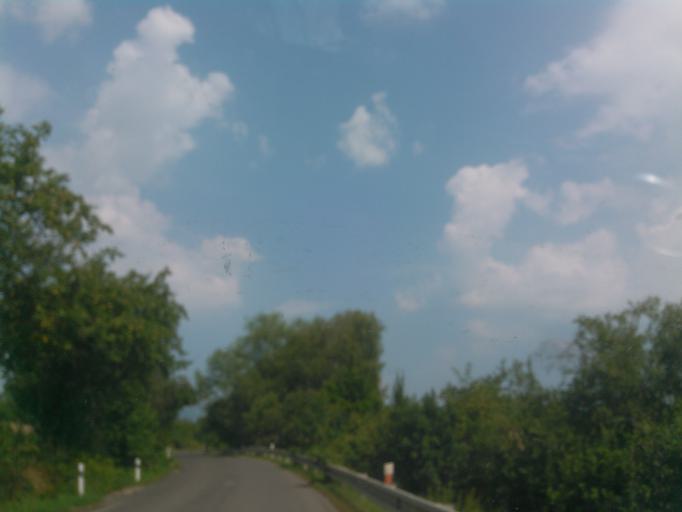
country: SK
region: Zilinsky
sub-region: Okres Liptovsky Mikulas
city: Liptovsky Mikulas
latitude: 49.0566
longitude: 19.4762
